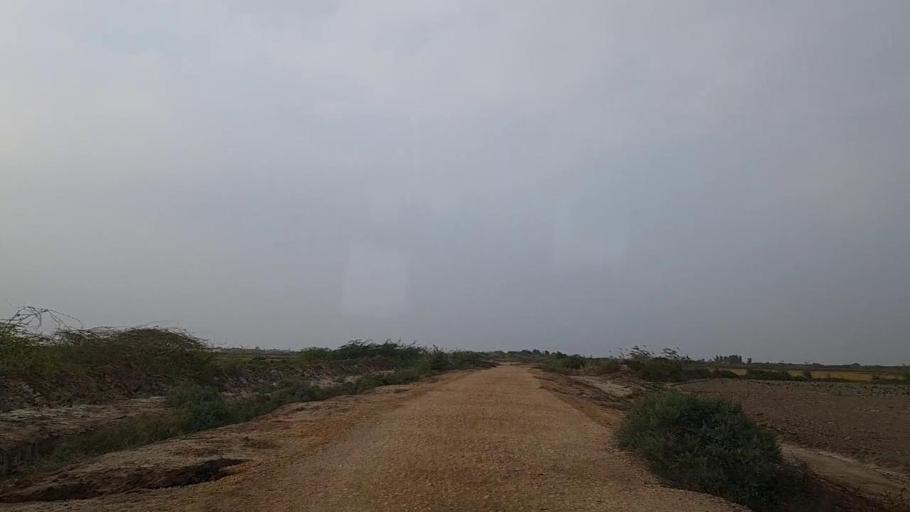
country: PK
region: Sindh
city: Mirpur Sakro
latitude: 24.6131
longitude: 67.5150
